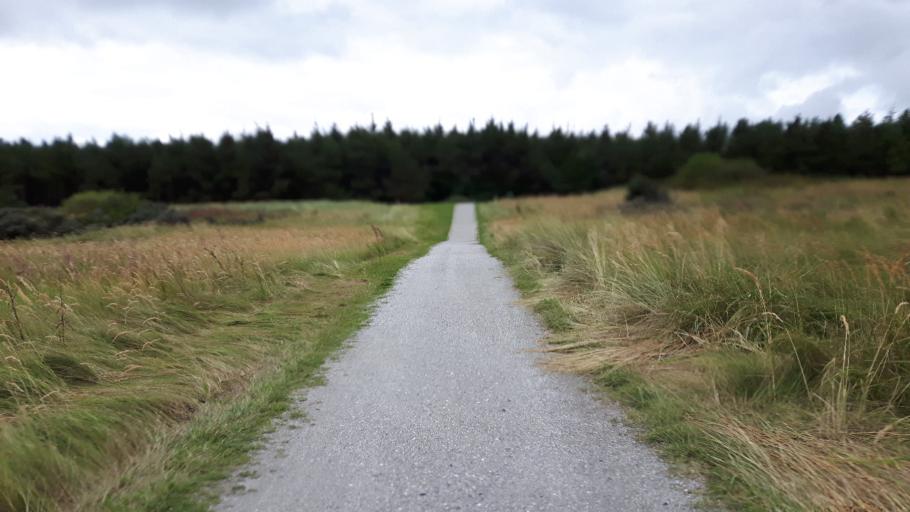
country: NL
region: Friesland
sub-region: Gemeente Ameland
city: Nes
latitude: 53.4536
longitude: 5.7150
